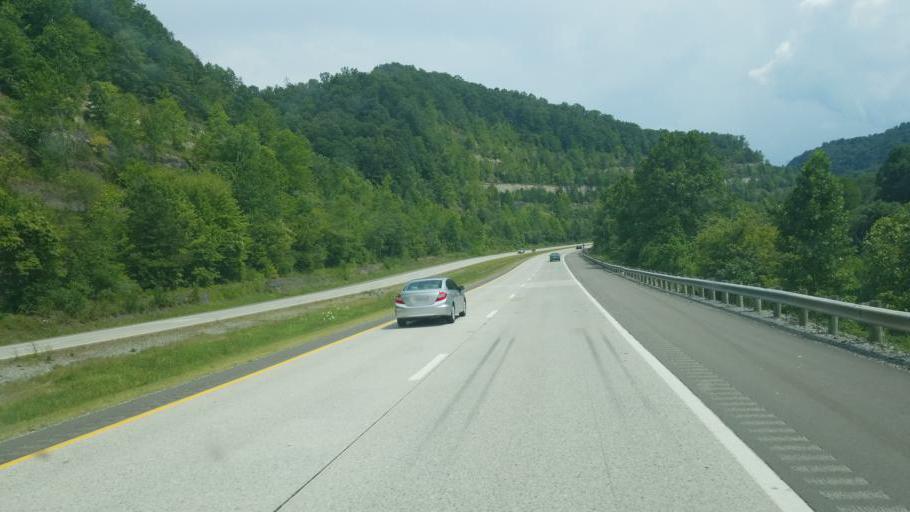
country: US
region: West Virginia
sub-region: Kanawha County
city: Alum Creek
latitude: 38.2156
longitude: -81.8321
